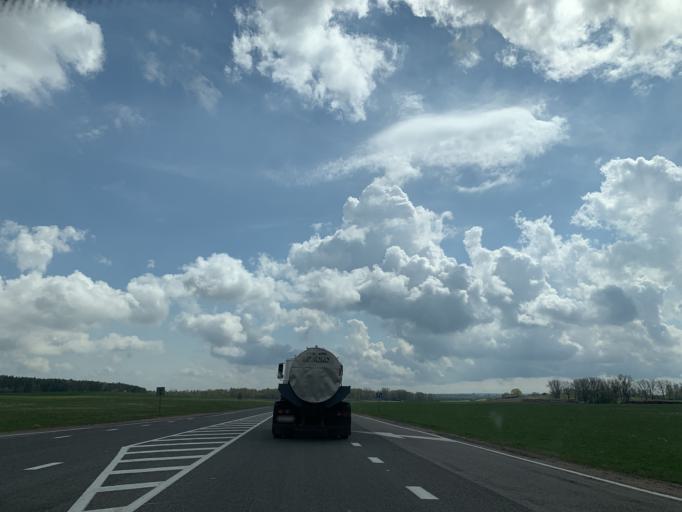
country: BY
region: Minsk
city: Nyasvizh
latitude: 53.2507
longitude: 26.6884
